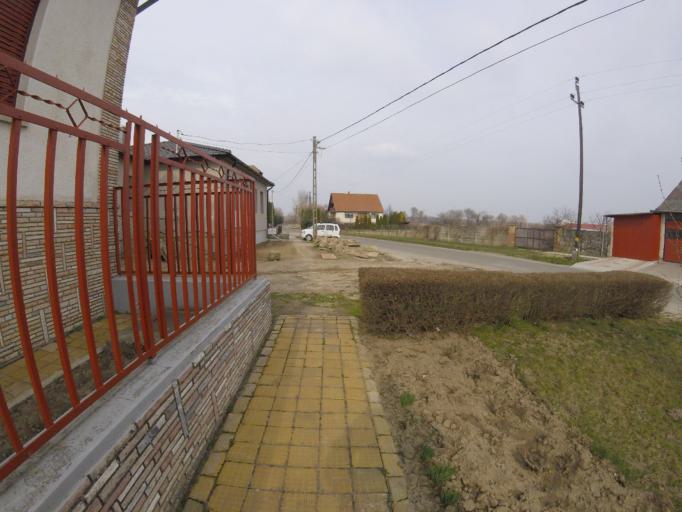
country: HU
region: Pest
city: Galgaheviz
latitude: 47.6236
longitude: 19.5520
